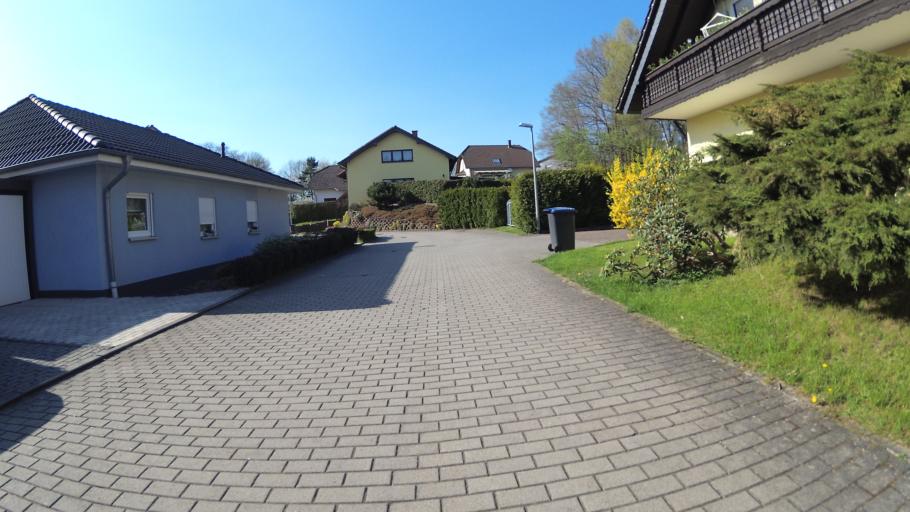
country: DE
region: Saarland
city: Merchweiler
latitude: 49.3566
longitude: 7.0679
